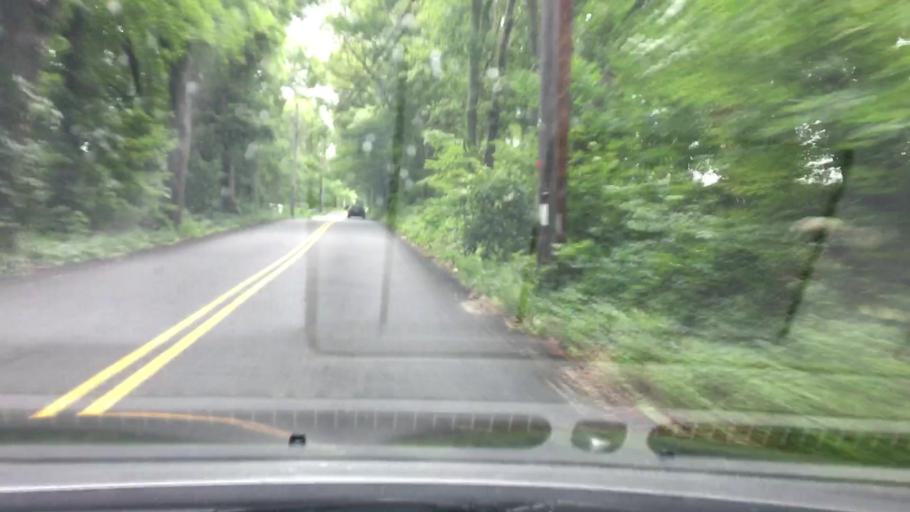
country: US
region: Rhode Island
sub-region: Providence County
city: Cumberland Hill
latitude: 42.0225
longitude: -71.4522
